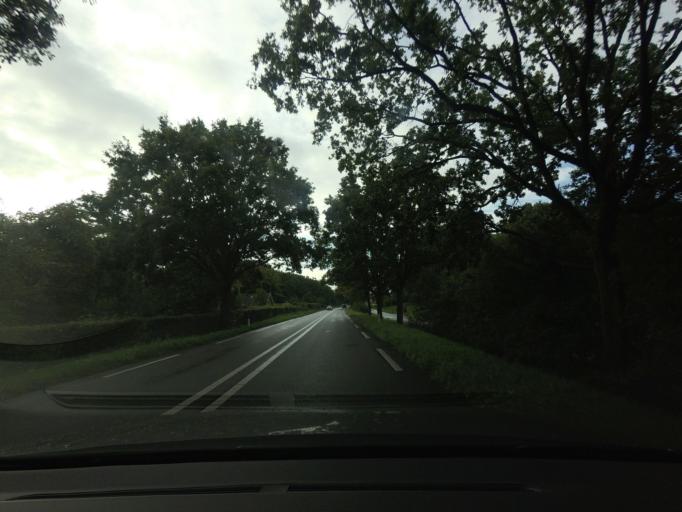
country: NL
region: South Holland
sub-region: Gemeente Wassenaar
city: Wassenaar
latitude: 52.1332
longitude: 4.4200
